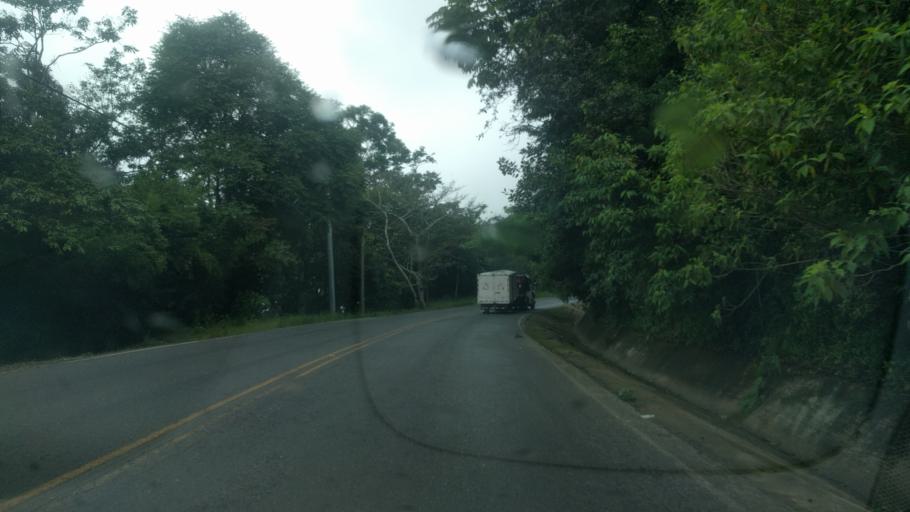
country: CR
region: Alajuela
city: San Rafael
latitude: 10.0333
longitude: -84.5123
